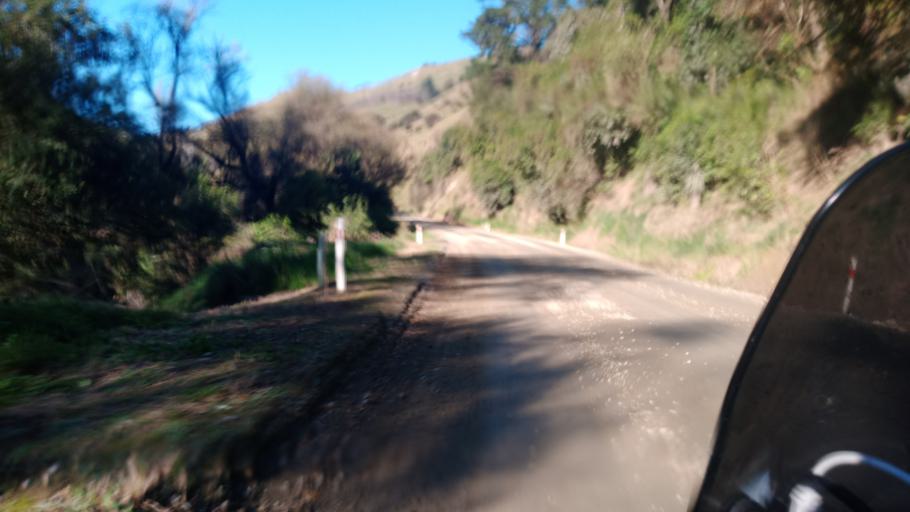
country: NZ
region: Hawke's Bay
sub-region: Wairoa District
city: Wairoa
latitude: -38.8464
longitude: 177.1659
